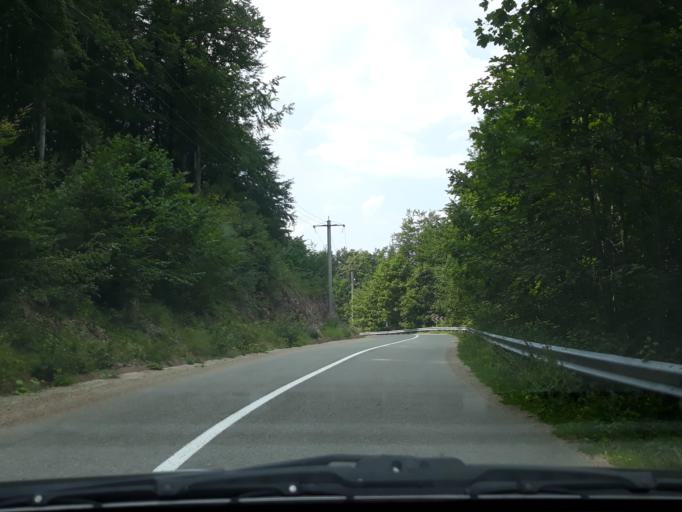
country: RO
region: Bihor
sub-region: Comuna Pietroasa
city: Pietroasa
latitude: 46.5931
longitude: 22.6804
